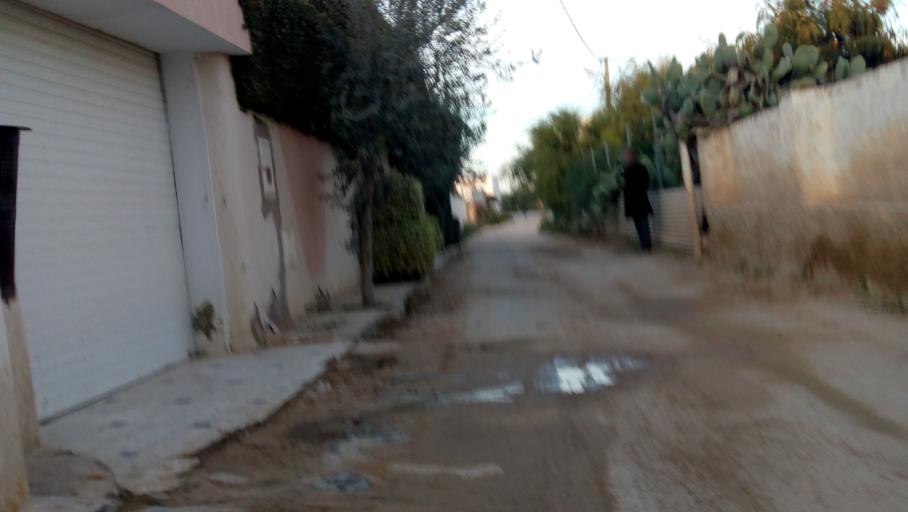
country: TN
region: Safaqis
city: Sfax
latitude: 34.7519
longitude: 10.7355
